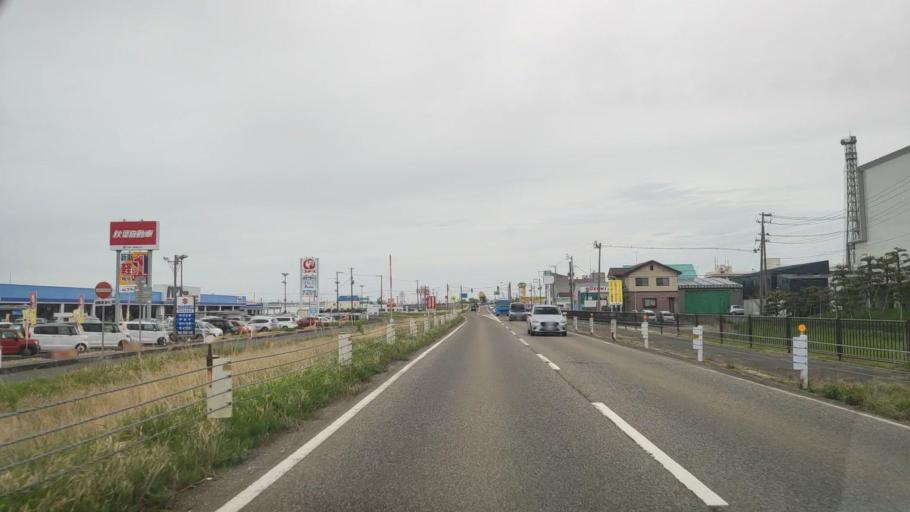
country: JP
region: Niigata
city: Niitsu-honcho
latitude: 37.7880
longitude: 139.1116
